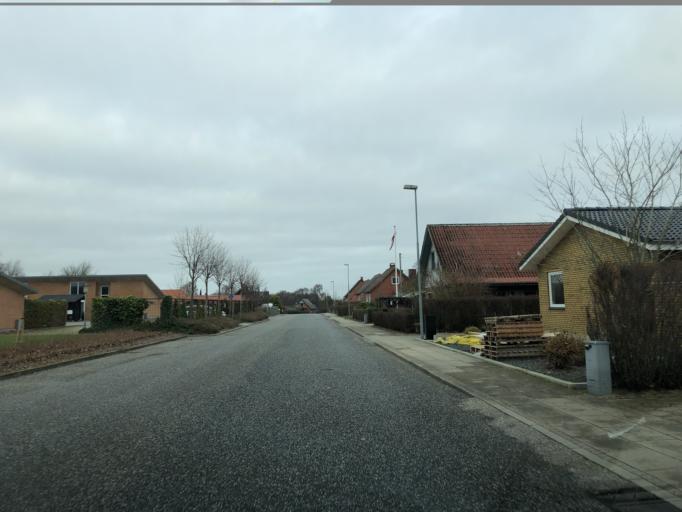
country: DK
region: Central Jutland
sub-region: Viborg Kommune
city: Stoholm
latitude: 56.4818
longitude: 9.1544
